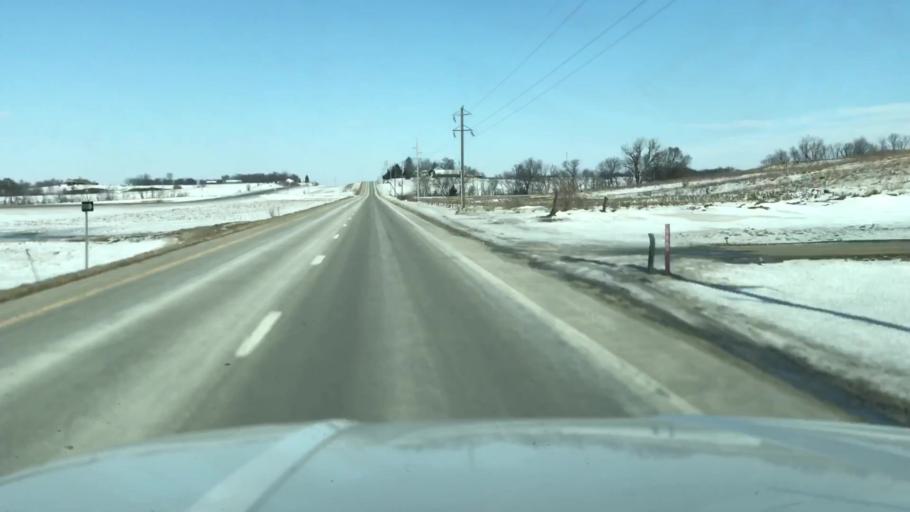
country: US
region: Missouri
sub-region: Nodaway County
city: Maryville
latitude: 40.1458
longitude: -94.8692
